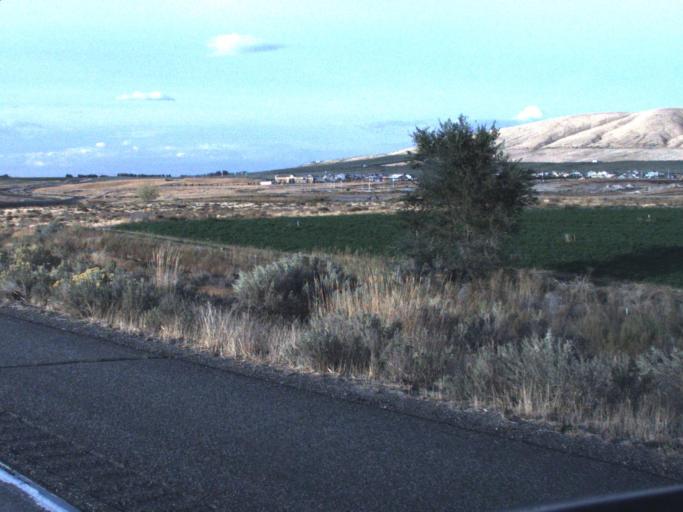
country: US
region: Washington
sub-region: Benton County
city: West Richland
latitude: 46.2130
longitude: -119.3446
